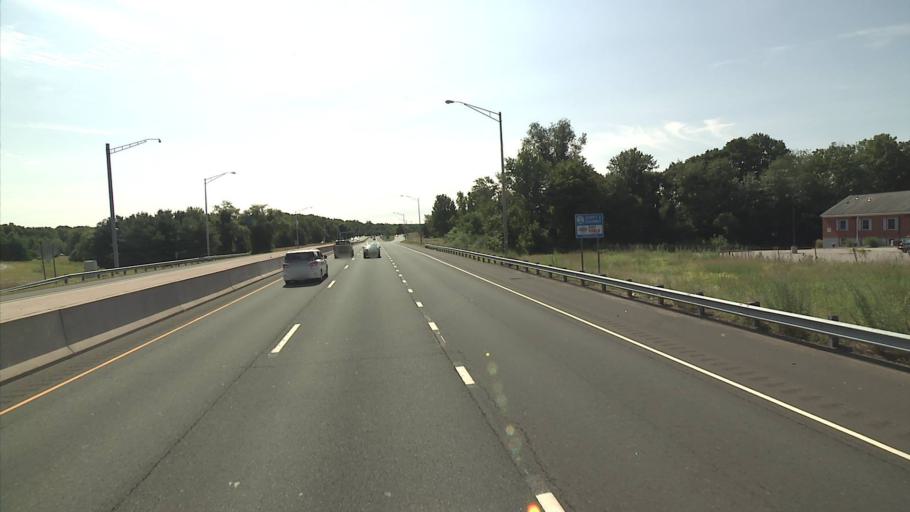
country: US
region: Connecticut
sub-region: Hartford County
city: Glastonbury
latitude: 41.7303
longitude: -72.6180
